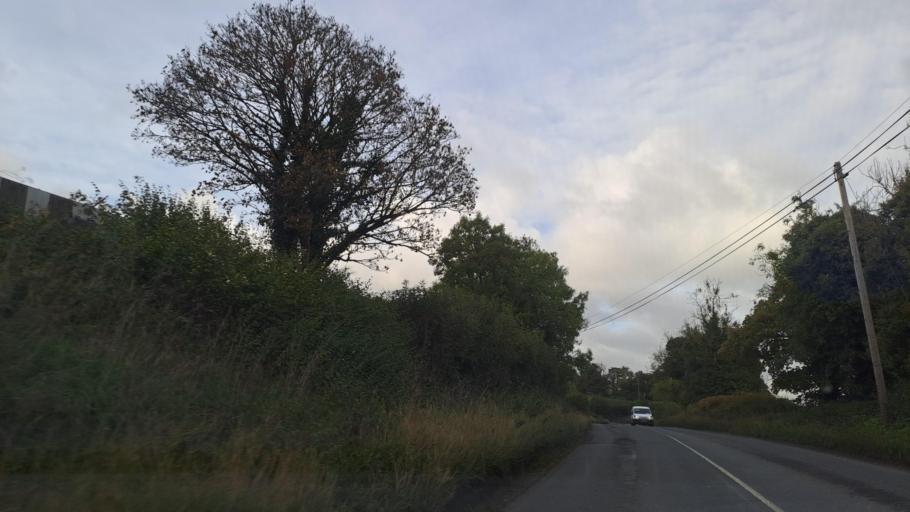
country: IE
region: Ulster
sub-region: An Cabhan
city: Kingscourt
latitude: 53.8821
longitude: -6.8038
